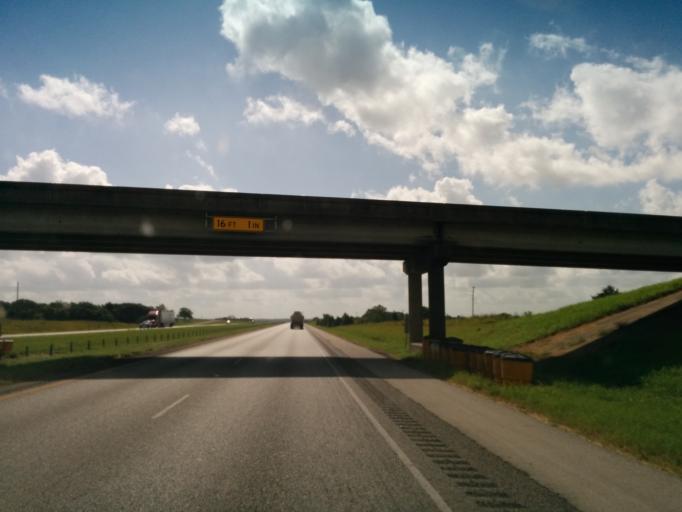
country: US
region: Texas
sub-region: Fayette County
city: Schulenburg
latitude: 29.6898
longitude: -96.9675
